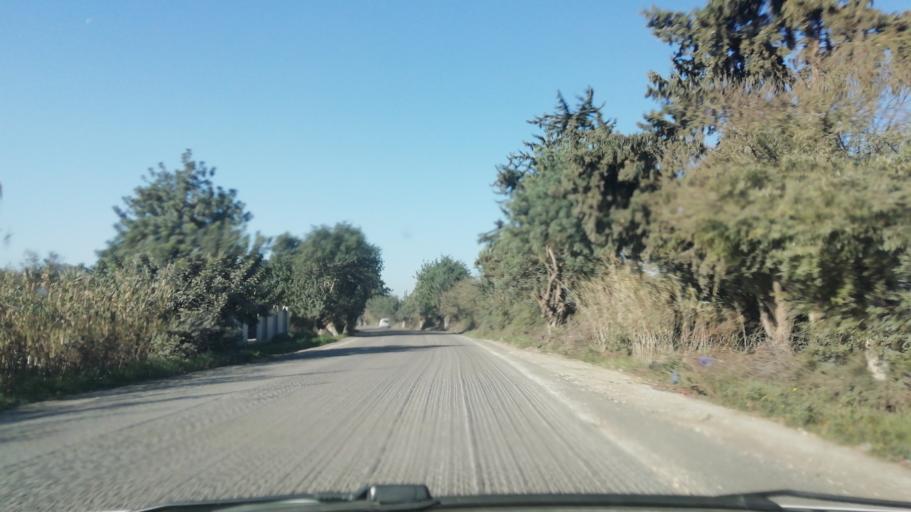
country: DZ
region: Mascara
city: Mascara
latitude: 35.5847
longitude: 0.0386
